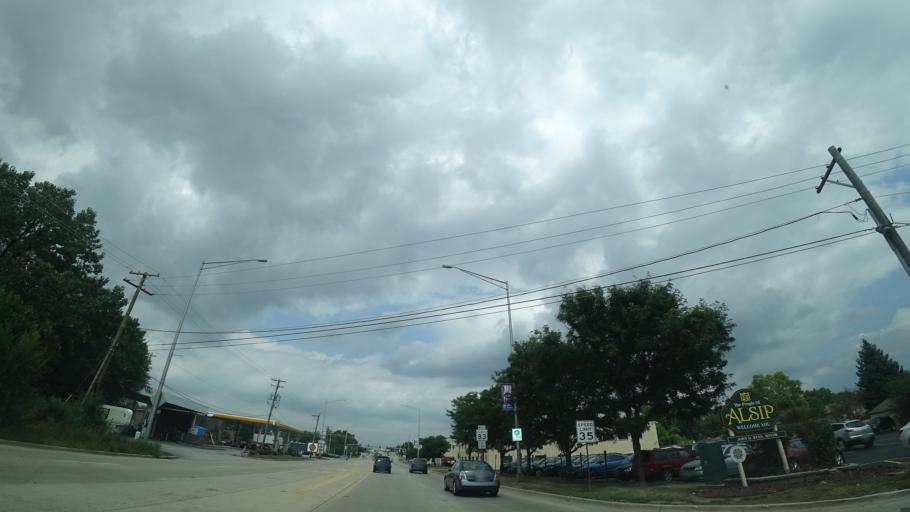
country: US
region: Illinois
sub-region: Cook County
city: Alsip
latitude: 41.6567
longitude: -87.7384
